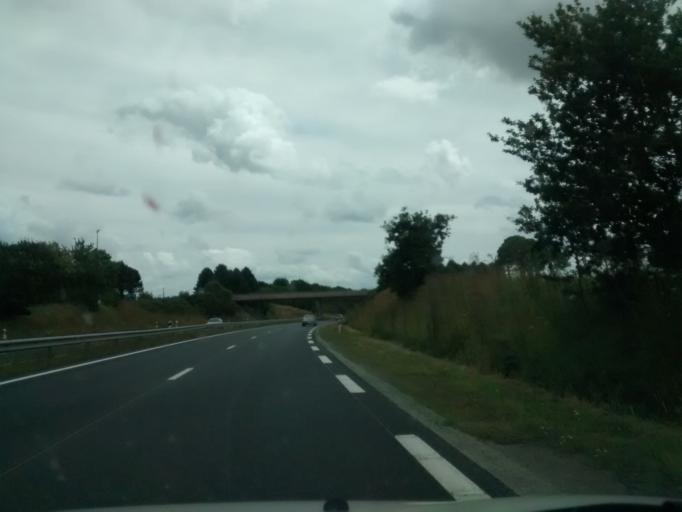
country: FR
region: Brittany
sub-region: Departement des Cotes-d'Armor
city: Pedernec
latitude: 48.5959
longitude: -3.2603
